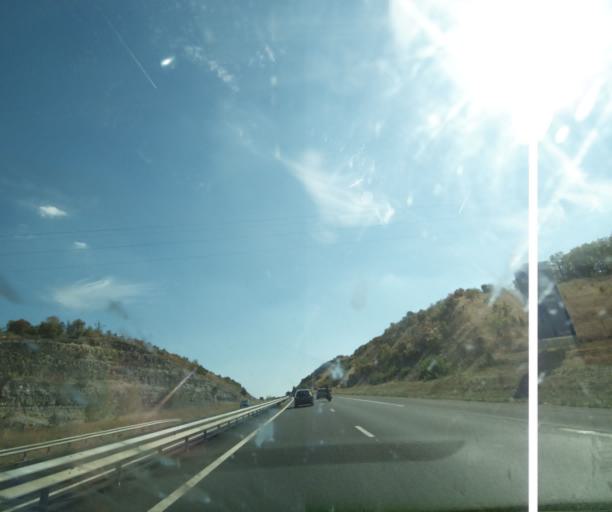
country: FR
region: Limousin
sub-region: Departement de la Correze
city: Brive-la-Gaillarde
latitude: 45.0589
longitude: 1.5071
